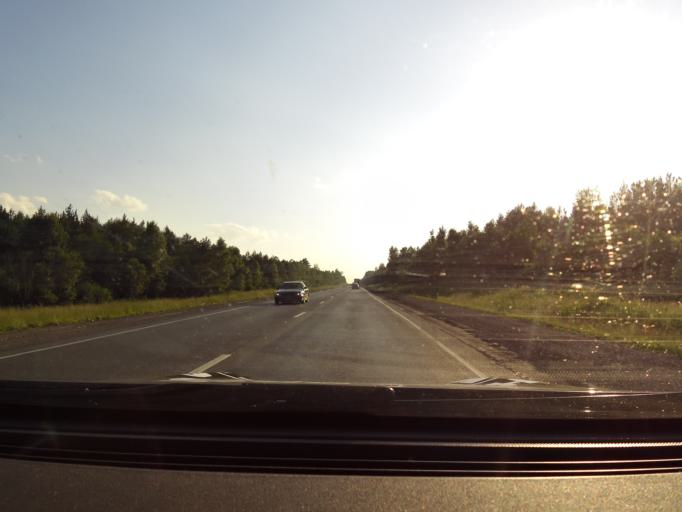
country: RU
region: Sverdlovsk
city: Druzhinino
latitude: 56.8308
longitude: 59.6181
